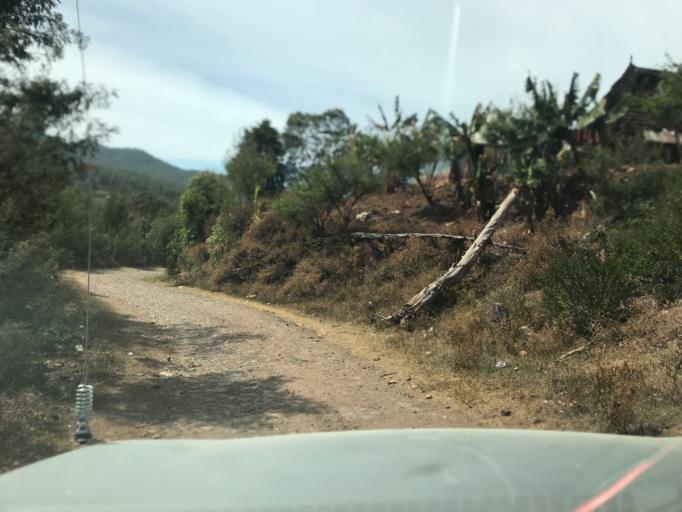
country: TL
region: Ainaro
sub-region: Ainaro
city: Ainaro
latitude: -8.8850
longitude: 125.5220
